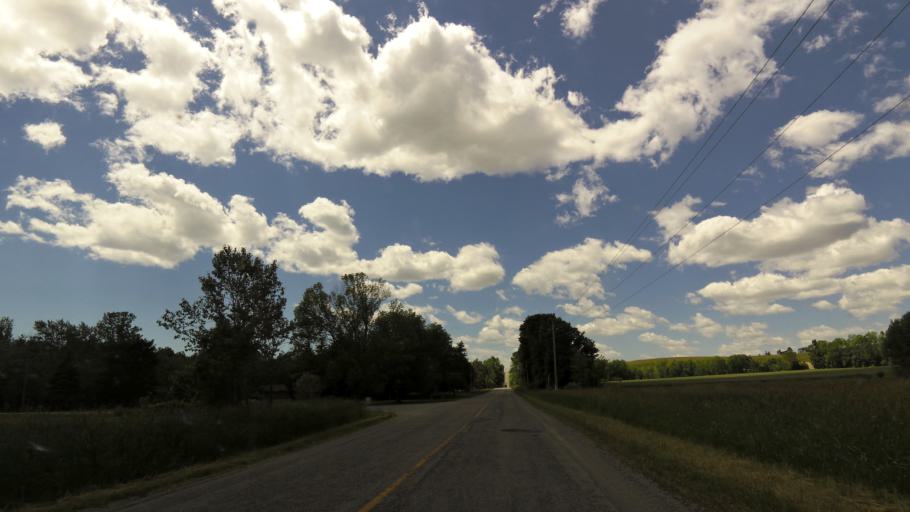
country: CA
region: Ontario
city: Oshawa
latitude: 43.9656
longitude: -78.5477
